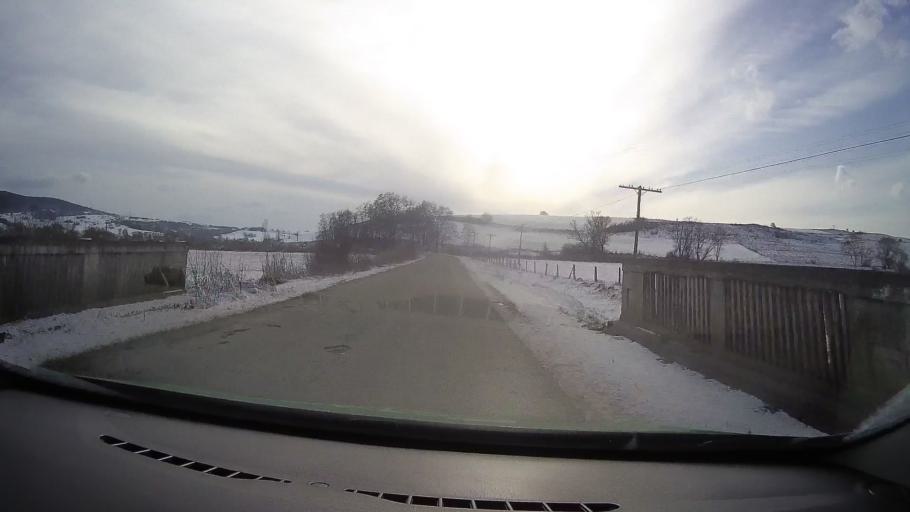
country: RO
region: Sibiu
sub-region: Comuna Iacobeni
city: Iacobeni
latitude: 46.0264
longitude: 24.7079
